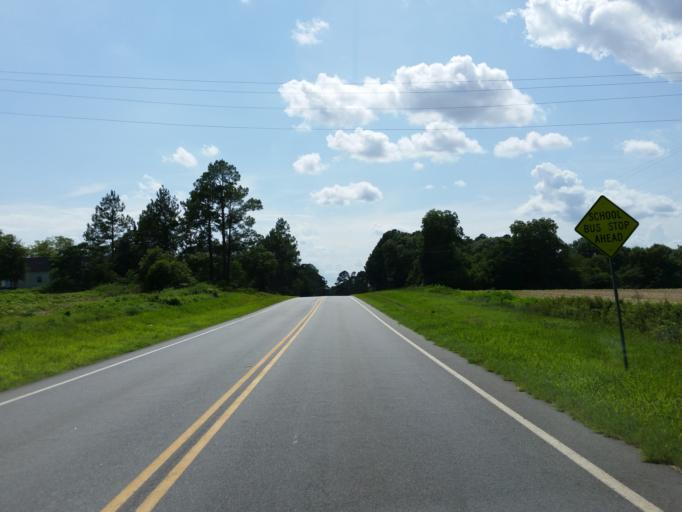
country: US
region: Georgia
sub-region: Turner County
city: Ashburn
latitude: 31.6589
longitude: -83.5874
